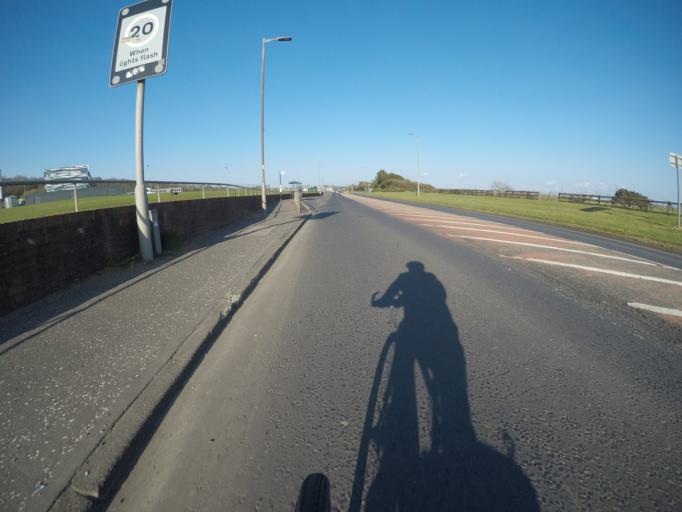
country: GB
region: Scotland
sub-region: North Ayrshire
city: Saltcoats
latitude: 55.6364
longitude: -4.7708
